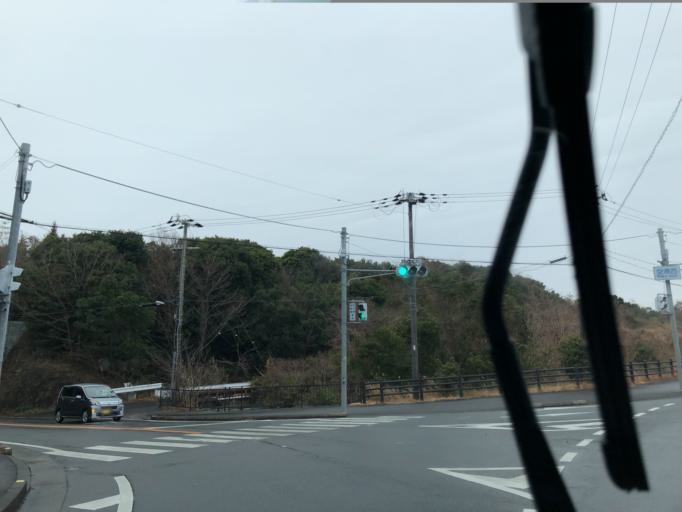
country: JP
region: Wakayama
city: Tanabe
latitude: 33.6667
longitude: 135.3566
